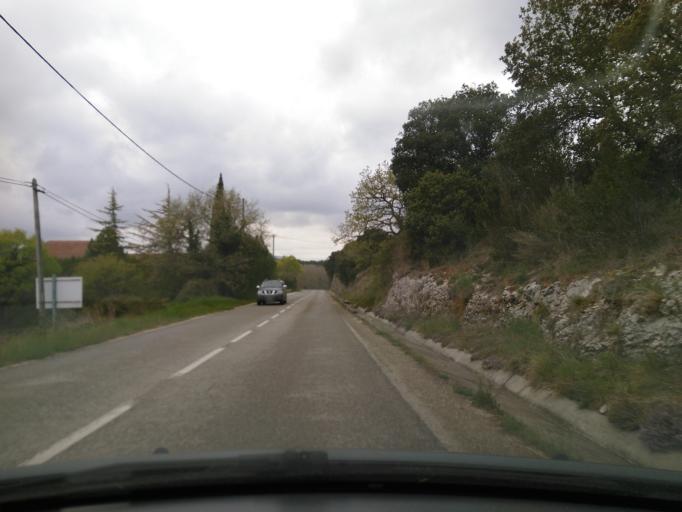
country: FR
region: Languedoc-Roussillon
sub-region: Departement du Gard
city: Barjac
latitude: 44.3517
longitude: 4.3973
